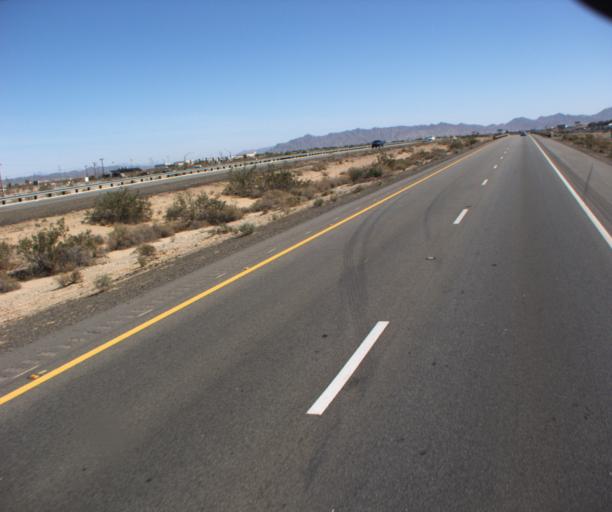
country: US
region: Arizona
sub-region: Yuma County
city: Yuma
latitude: 32.6771
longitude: -114.5246
